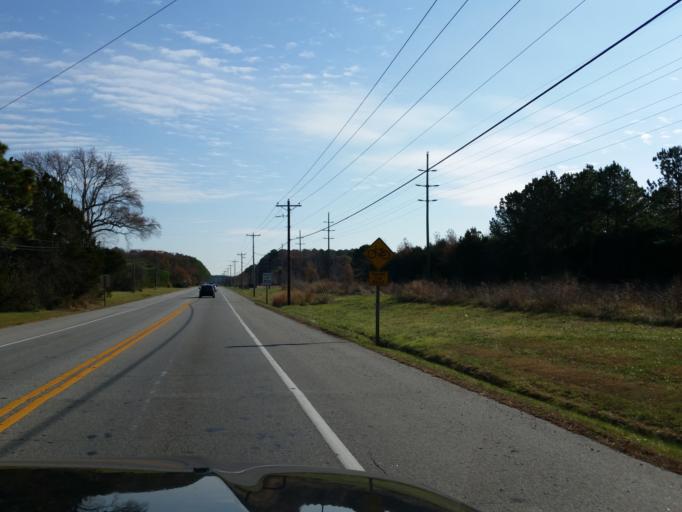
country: US
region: Maryland
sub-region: Talbot County
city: Saint Michaels
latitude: 38.7686
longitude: -76.2049
